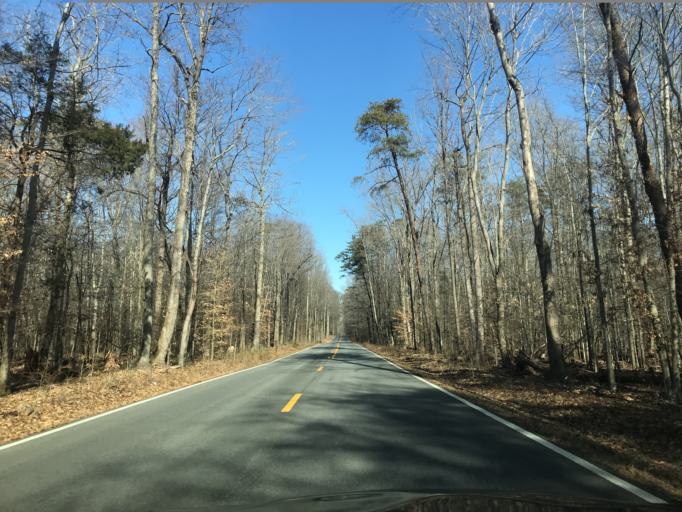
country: US
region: Virginia
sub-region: Prince William County
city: Quantico Station
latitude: 38.4919
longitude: -77.2550
